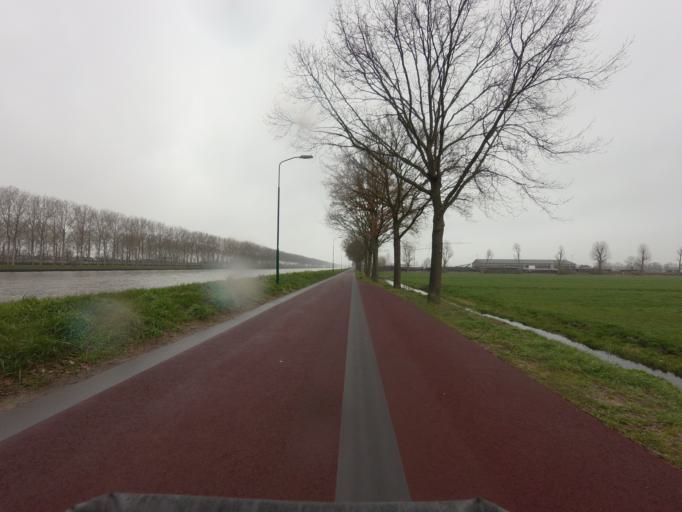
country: NL
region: Utrecht
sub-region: Stichtse Vecht
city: Spechtenkamp
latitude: 52.1410
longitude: 5.0273
